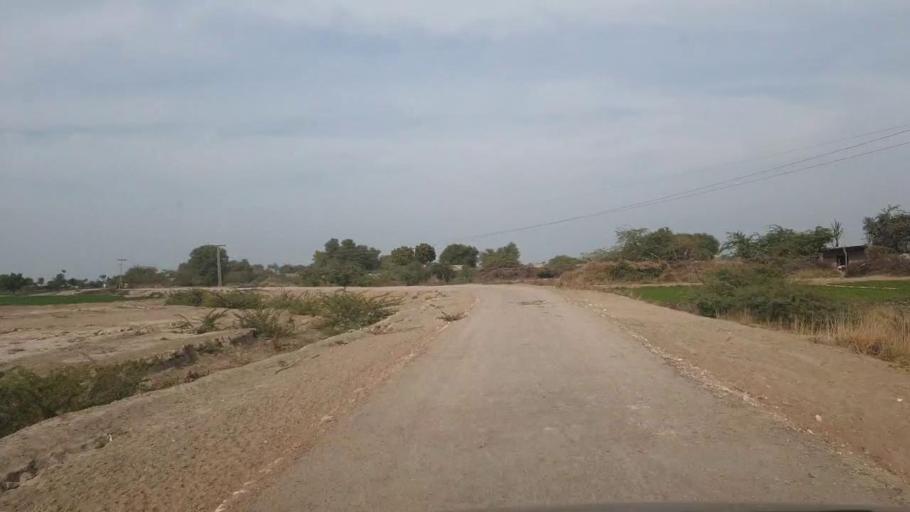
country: PK
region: Sindh
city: Shahpur Chakar
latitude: 26.1060
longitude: 68.5055
